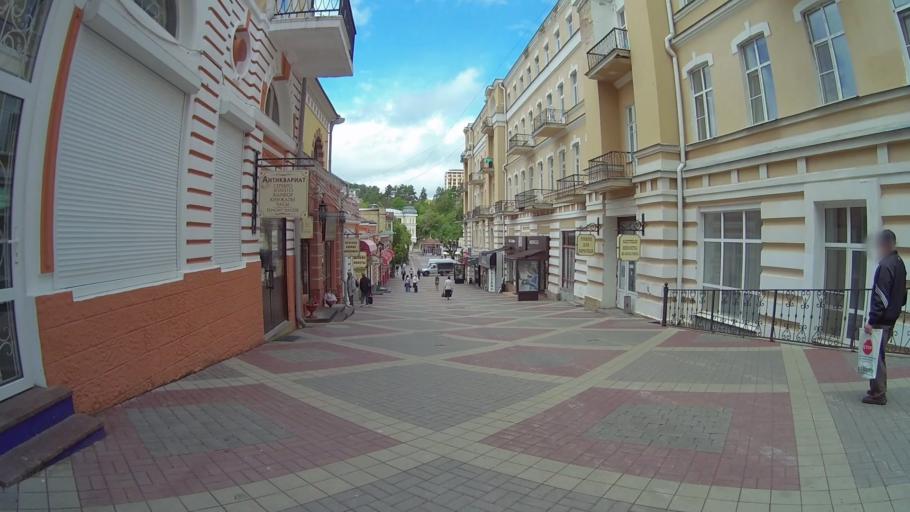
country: RU
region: Stavropol'skiy
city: Kislovodsk
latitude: 43.9008
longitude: 42.7185
